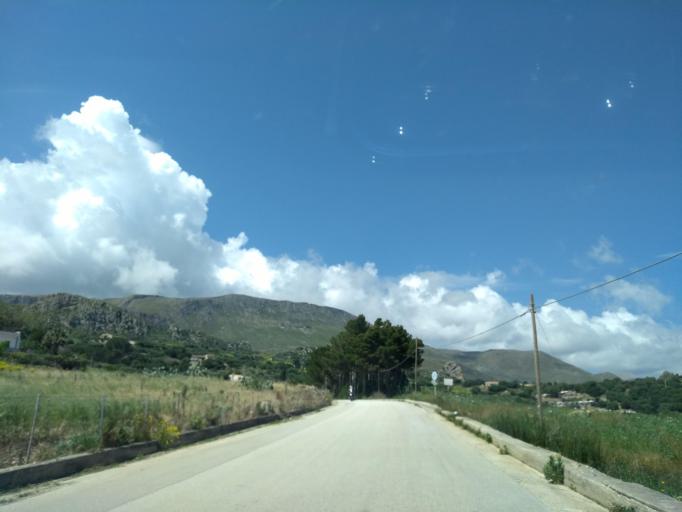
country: IT
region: Sicily
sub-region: Trapani
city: Castellammare del Golfo
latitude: 38.0648
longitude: 12.8224
